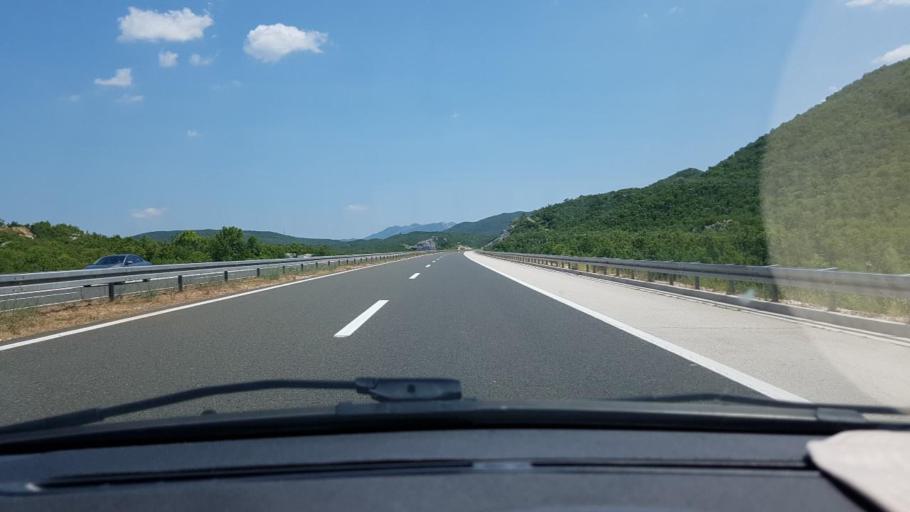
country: HR
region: Splitsko-Dalmatinska
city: Grubine
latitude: 43.3595
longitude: 17.1027
